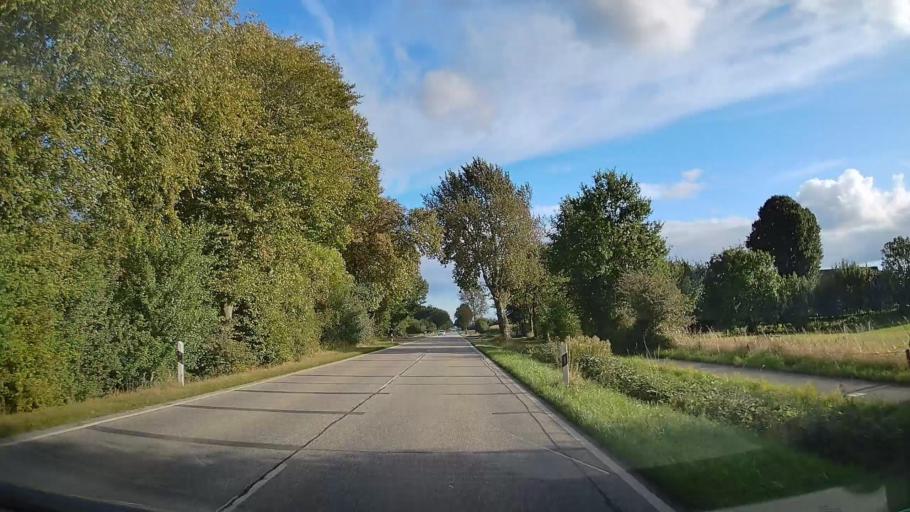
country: DE
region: Schleswig-Holstein
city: Rabel
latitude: 54.7322
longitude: 9.9419
